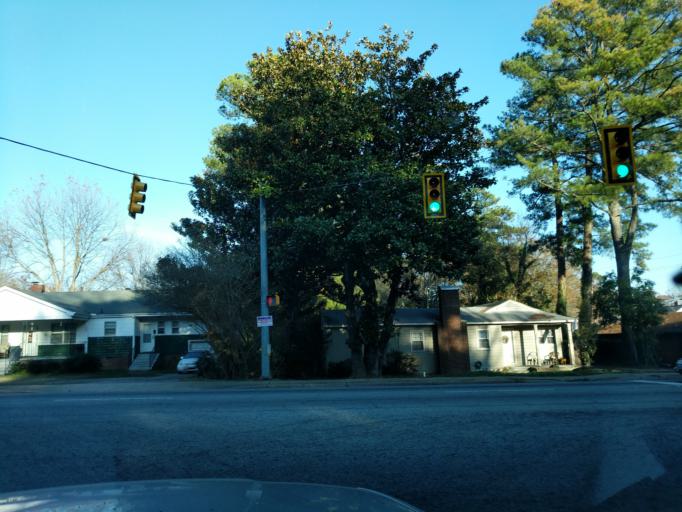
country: US
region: South Carolina
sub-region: Spartanburg County
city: Saxon
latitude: 34.9820
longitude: -81.9450
